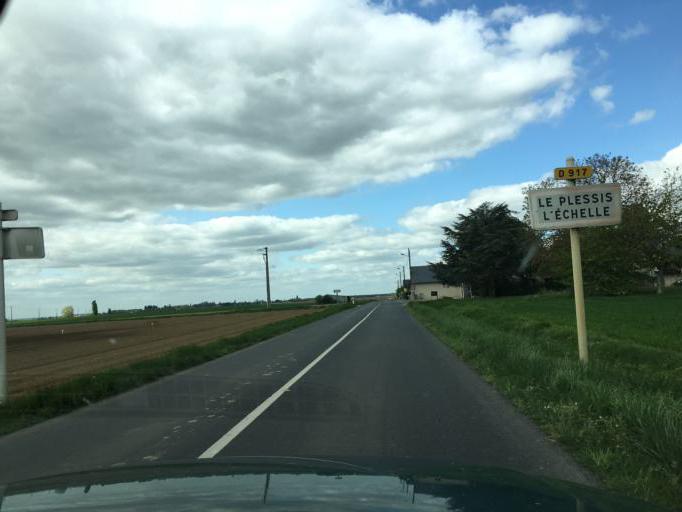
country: FR
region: Centre
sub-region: Departement du Loir-et-Cher
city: Mer
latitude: 47.8123
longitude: 1.4296
